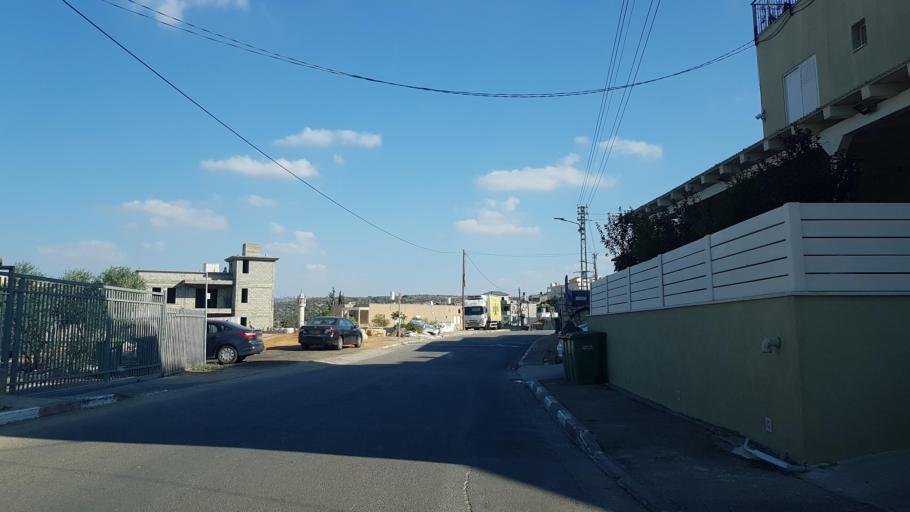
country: PS
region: West Bank
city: Zayta
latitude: 32.3683
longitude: 35.0432
